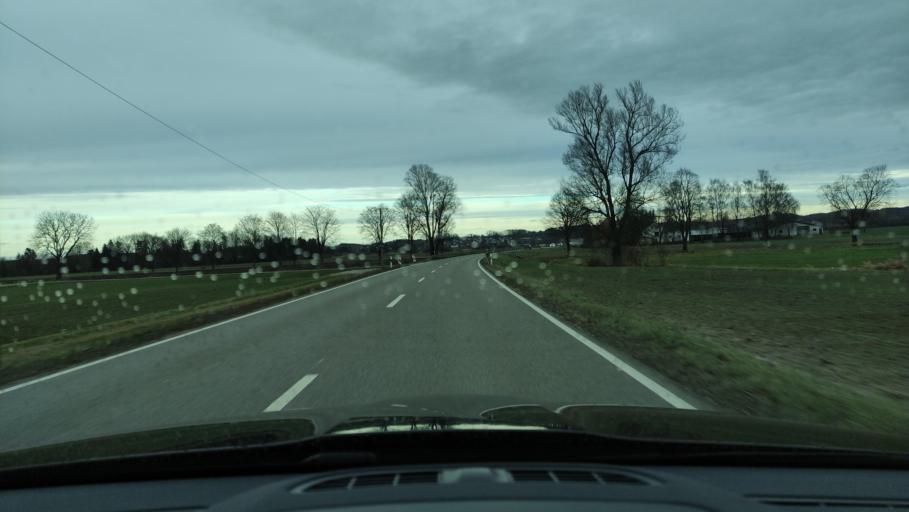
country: DE
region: Bavaria
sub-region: Swabia
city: Illertissen
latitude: 48.2284
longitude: 10.1413
